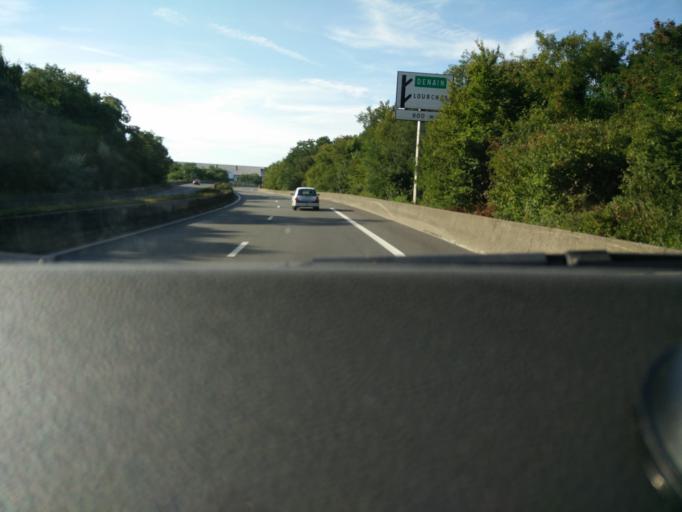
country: FR
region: Nord-Pas-de-Calais
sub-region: Departement du Nord
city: Lourches
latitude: 50.3123
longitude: 3.3710
